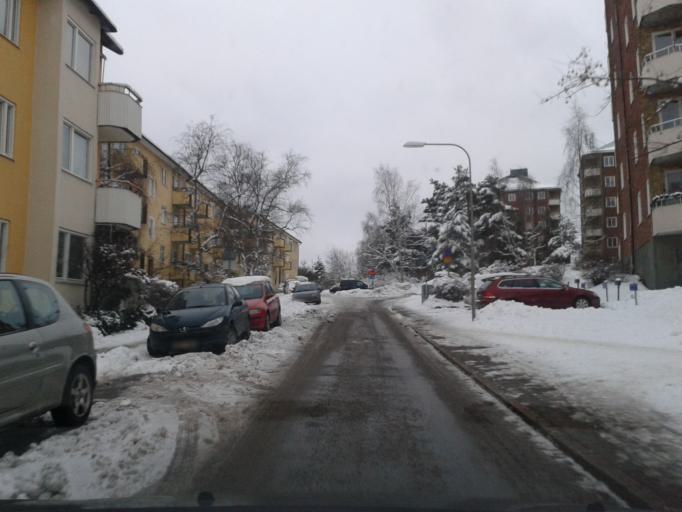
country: SE
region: Stockholm
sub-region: Stockholms Kommun
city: Arsta
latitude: 59.2689
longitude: 18.0465
